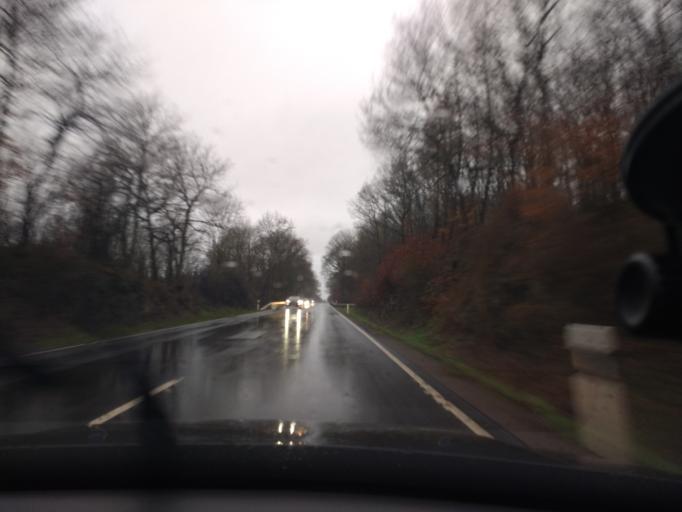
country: DE
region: Rheinland-Pfalz
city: Pellingen
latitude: 49.6993
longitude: 6.6408
